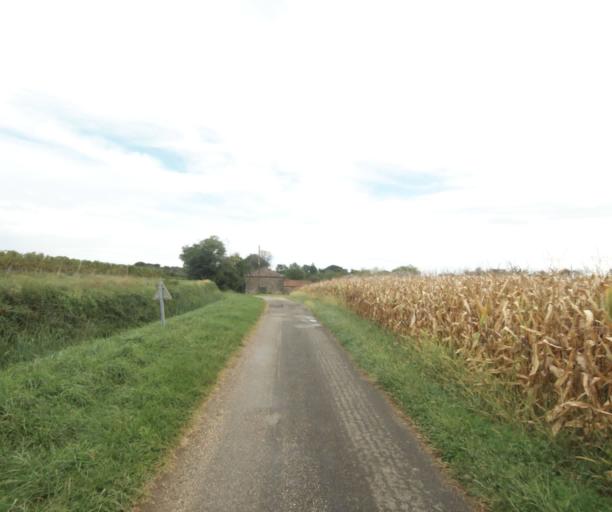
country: FR
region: Midi-Pyrenees
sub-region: Departement du Gers
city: Cazaubon
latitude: 43.8962
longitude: -0.1535
